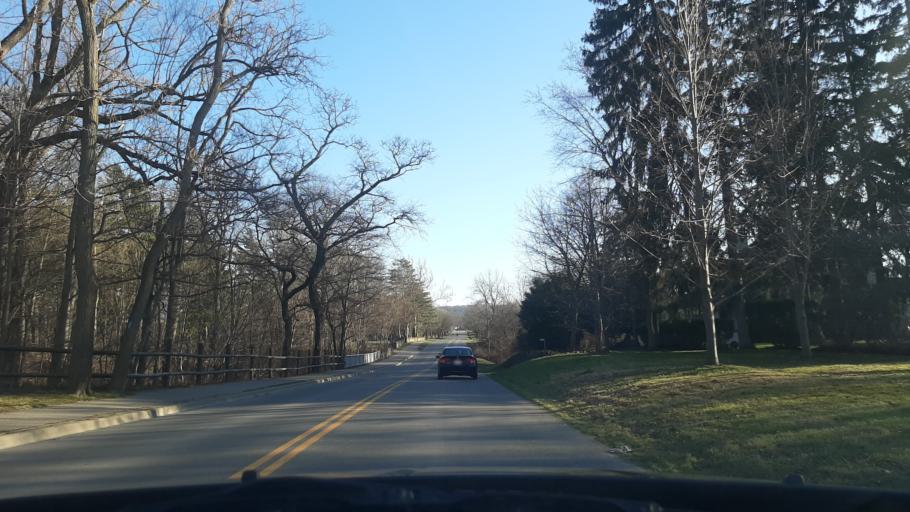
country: US
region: New York
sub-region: Niagara County
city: Lewiston
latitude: 43.1805
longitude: -79.0583
